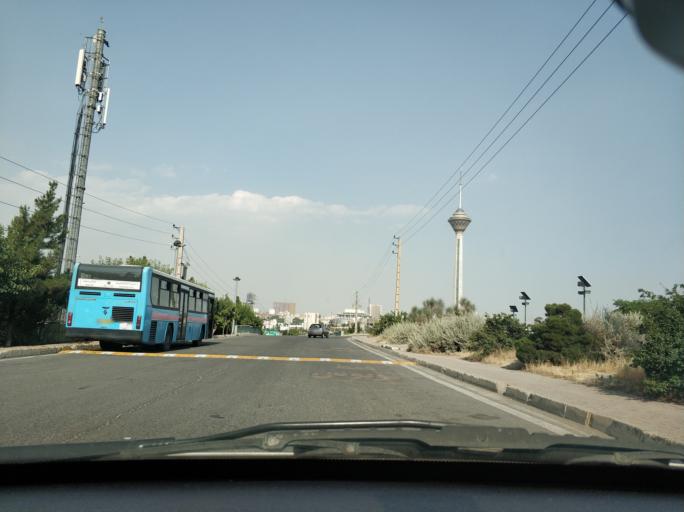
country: IR
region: Tehran
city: Tehran
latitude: 35.7493
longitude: 51.3601
